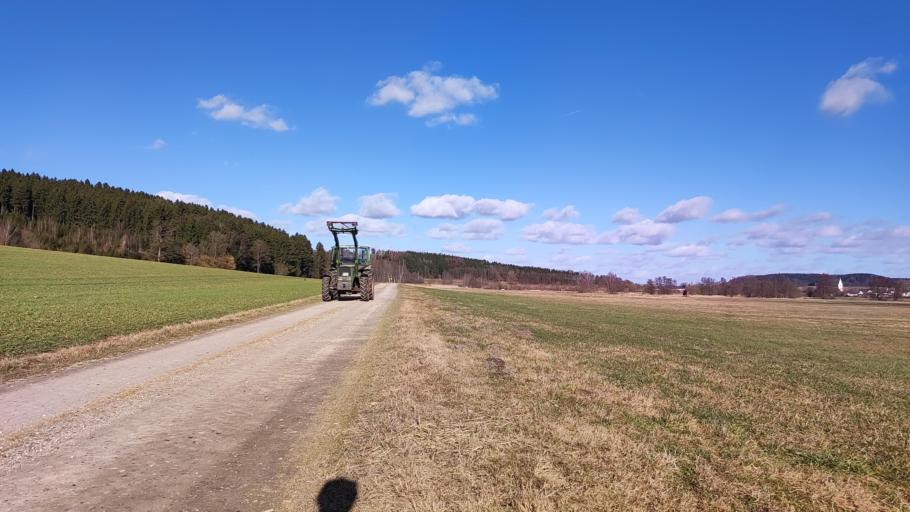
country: DE
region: Bavaria
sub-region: Swabia
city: Zusmarshausen
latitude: 48.4248
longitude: 10.5902
